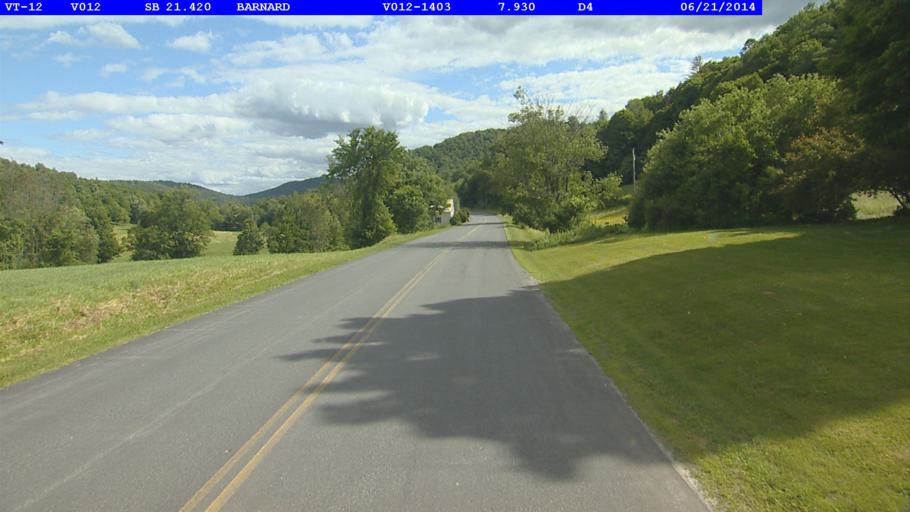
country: US
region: Vermont
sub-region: Orange County
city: Randolph
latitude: 43.7698
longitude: -72.6370
